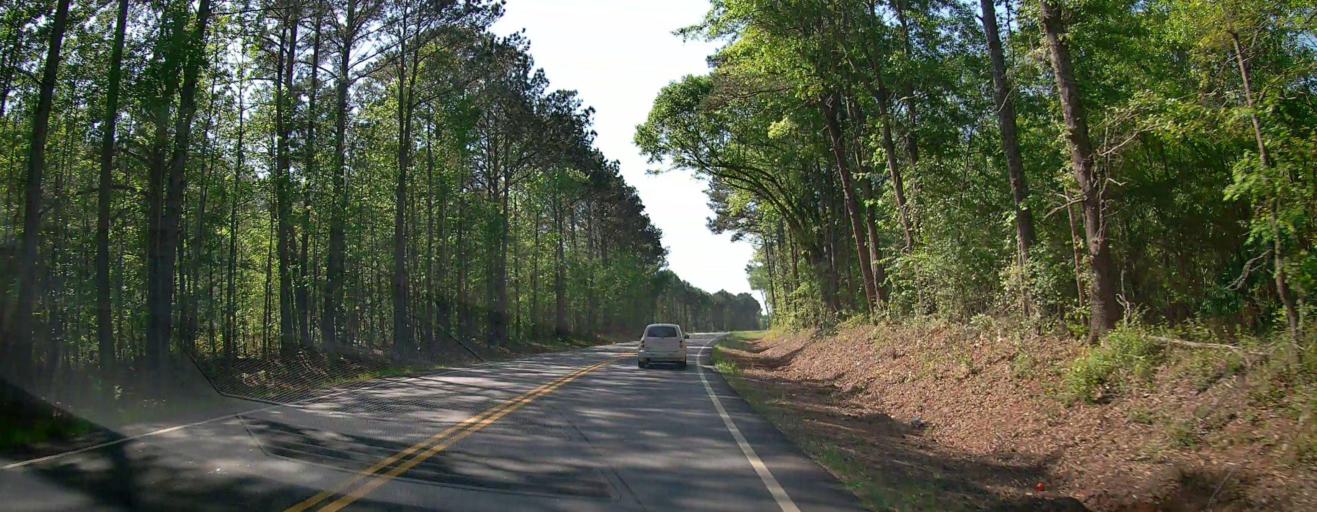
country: US
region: Georgia
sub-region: Morgan County
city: Madison
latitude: 33.6003
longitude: -83.4201
